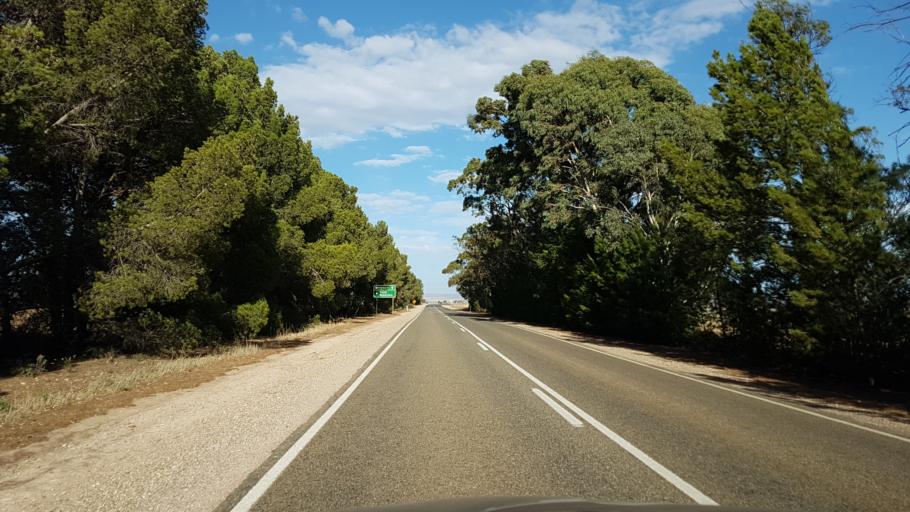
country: AU
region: South Australia
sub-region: Clare and Gilbert Valleys
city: Clare
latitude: -33.6943
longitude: 138.4216
